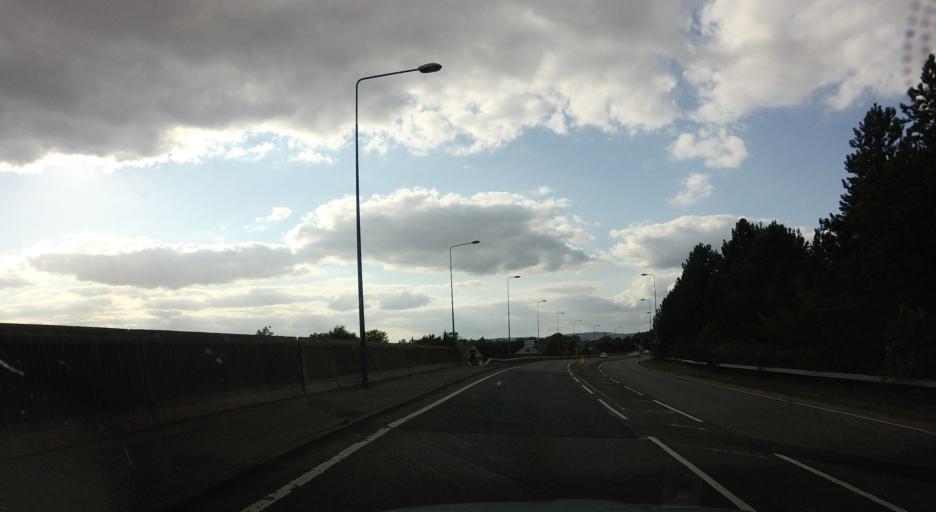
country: GB
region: Scotland
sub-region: Angus
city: Muirhead
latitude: 56.4588
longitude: -3.0503
